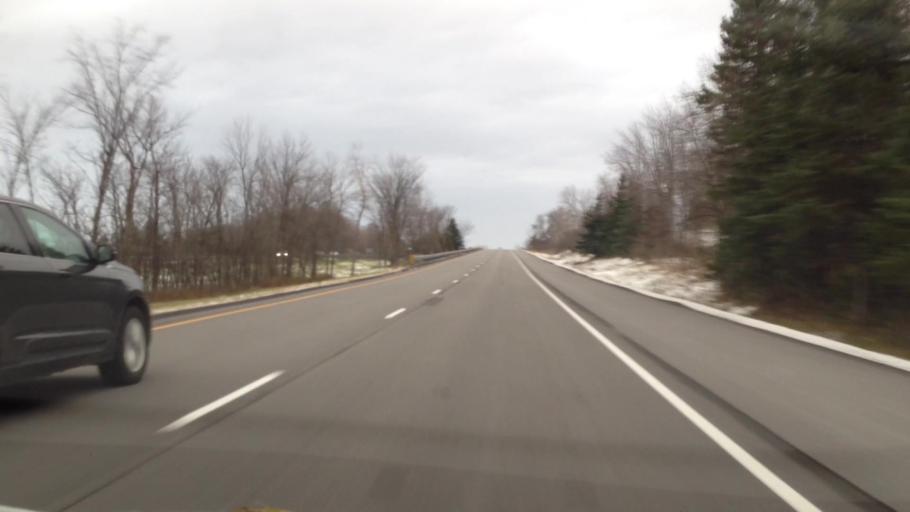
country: CA
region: Quebec
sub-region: Monteregie
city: Rigaud
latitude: 45.5421
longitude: -74.4031
